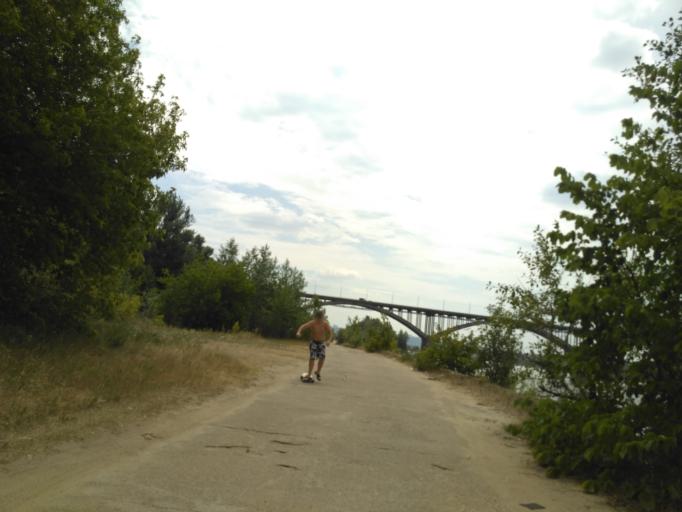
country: RU
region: Nizjnij Novgorod
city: Nizhniy Novgorod
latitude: 56.3034
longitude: 43.9677
